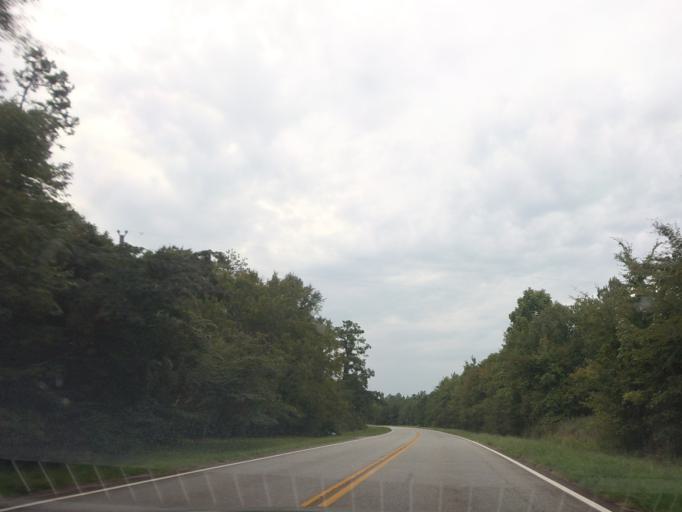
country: US
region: Georgia
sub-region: Twiggs County
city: Jeffersonville
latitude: 32.7338
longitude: -83.4202
